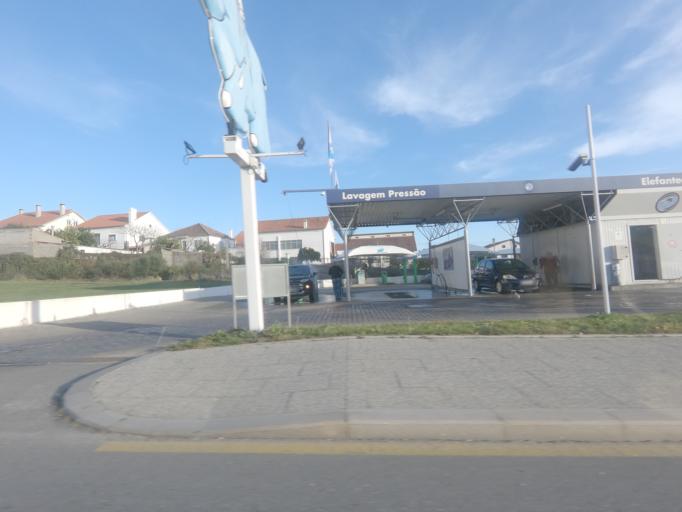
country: PT
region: Castelo Branco
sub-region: Castelo Branco
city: Castelo Branco
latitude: 39.8120
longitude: -7.5068
